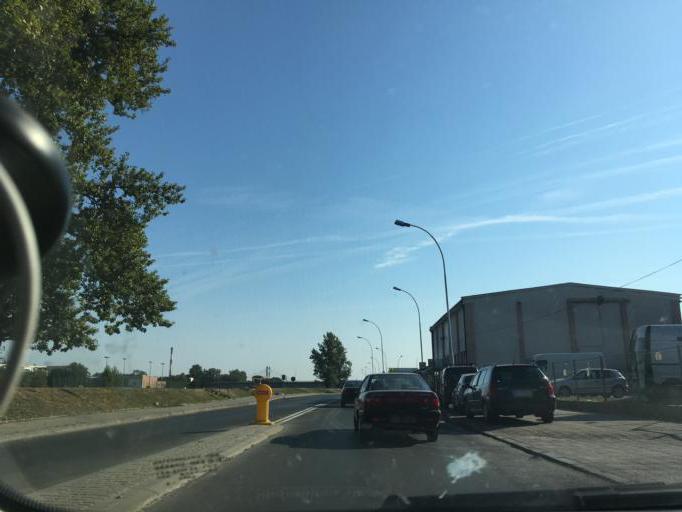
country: PL
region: Subcarpathian Voivodeship
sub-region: Przemysl
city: Przemysl
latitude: 49.7856
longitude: 22.7720
